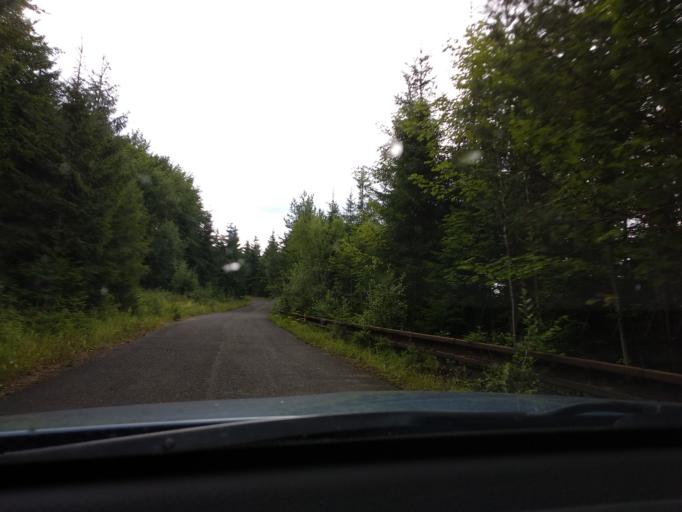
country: SK
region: Zilinsky
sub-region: Okres Liptovsky Mikulas
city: Hybe
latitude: 49.0278
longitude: 19.8880
